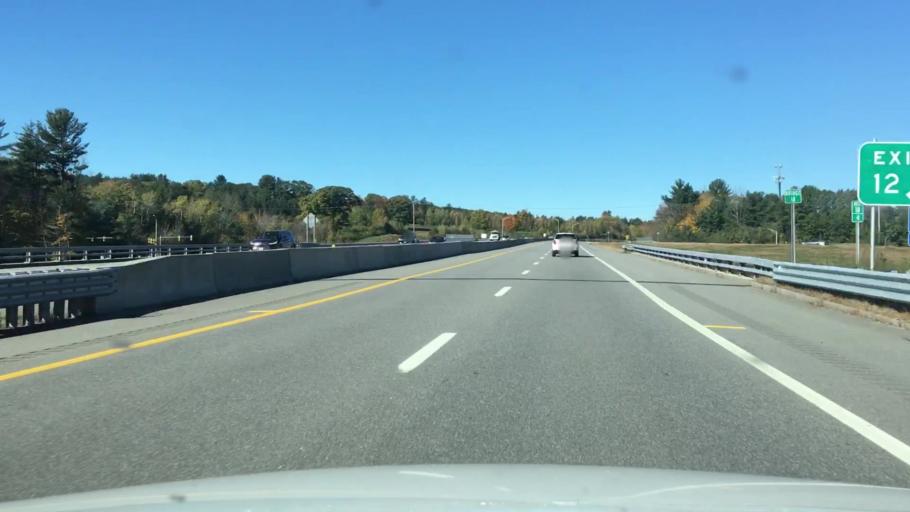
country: US
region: New Hampshire
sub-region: Strafford County
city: Rochester
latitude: 43.2816
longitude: -70.9770
